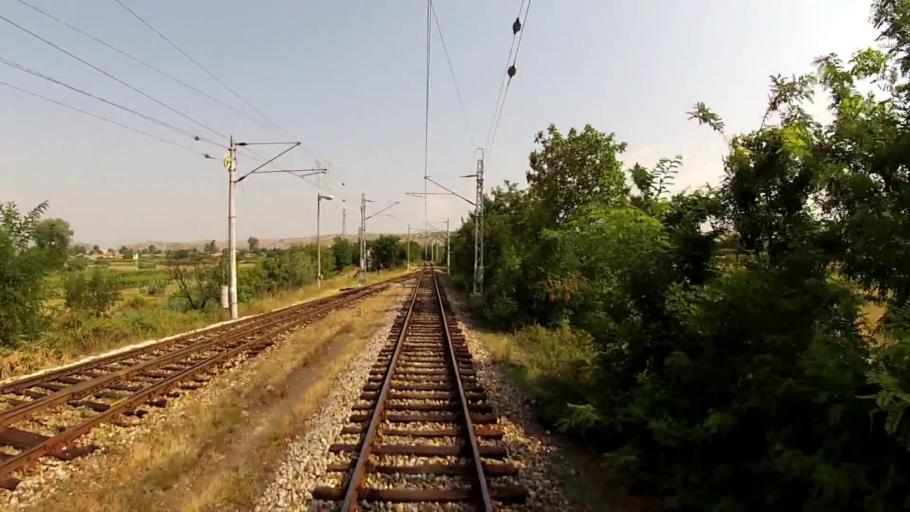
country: BG
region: Blagoevgrad
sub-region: Obshtina Petrich
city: Petrich
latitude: 41.4054
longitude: 23.3555
